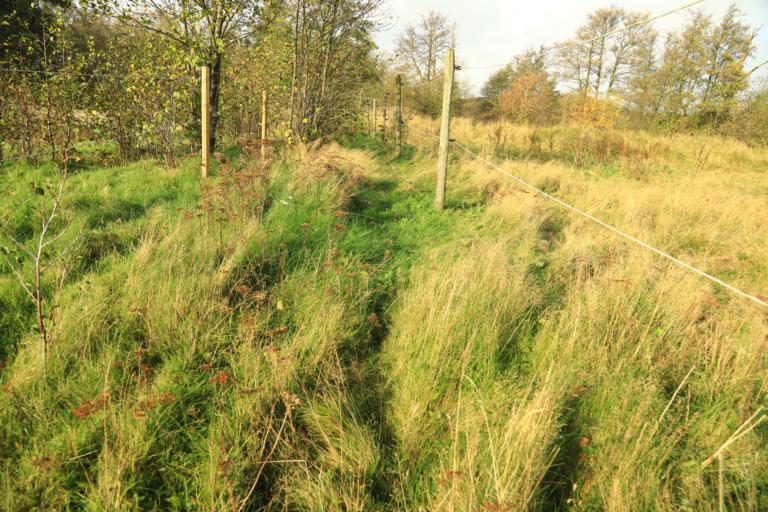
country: SE
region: Halland
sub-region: Varbergs Kommun
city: Varberg
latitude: 57.1301
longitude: 12.2894
